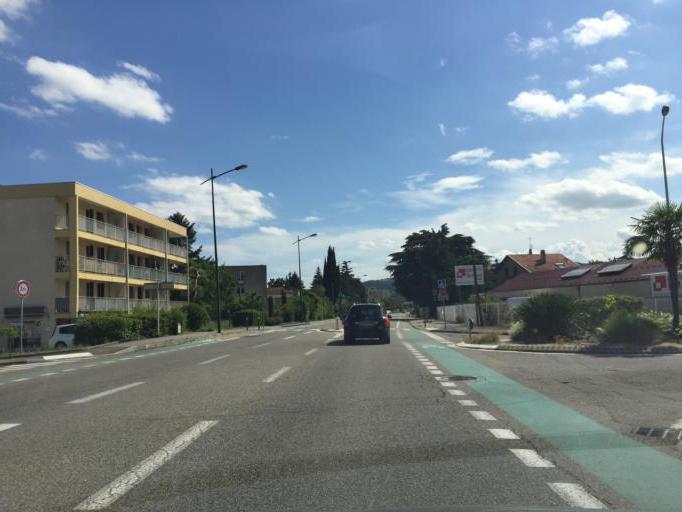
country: FR
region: Rhone-Alpes
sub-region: Departement de l'Ardeche
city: Tournon-sur-Rhone
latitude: 45.0596
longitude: 4.8415
